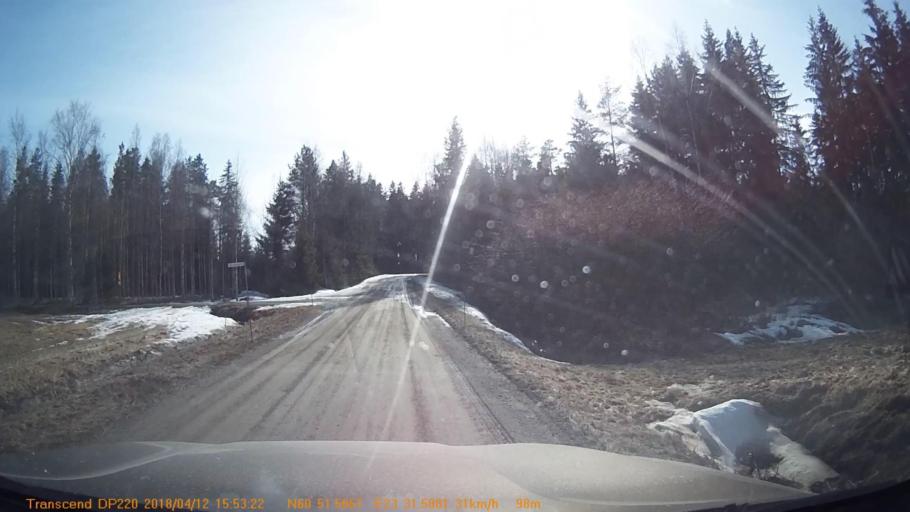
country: FI
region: Haeme
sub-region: Forssa
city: Jokioinen
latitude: 60.8597
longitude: 23.5264
